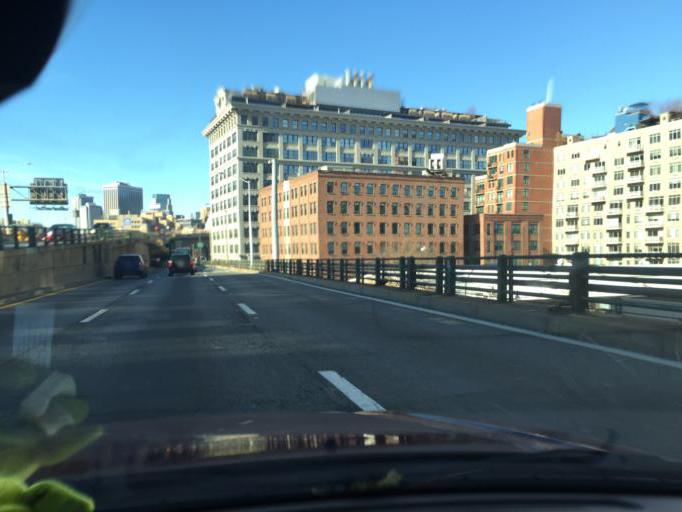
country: US
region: New York
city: New York City
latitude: 40.7012
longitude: -73.9882
